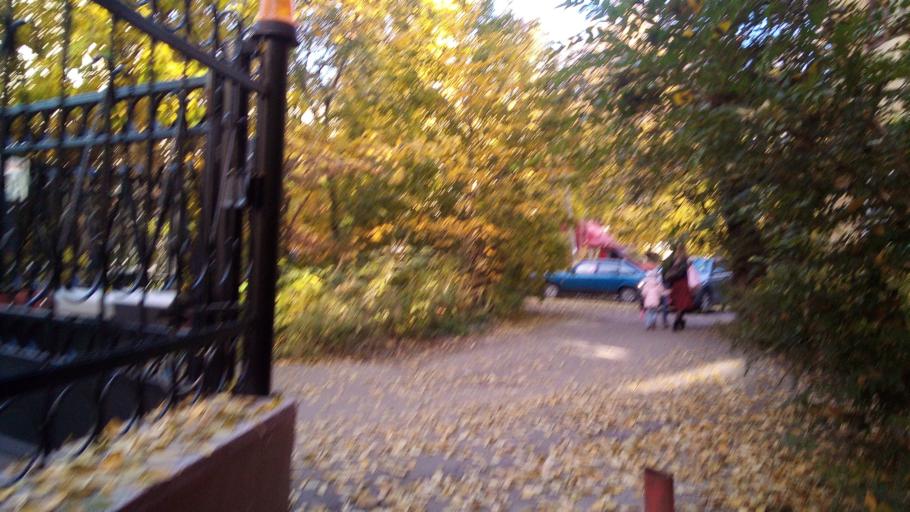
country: RU
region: Chelyabinsk
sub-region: Gorod Chelyabinsk
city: Chelyabinsk
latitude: 55.1546
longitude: 61.4126
